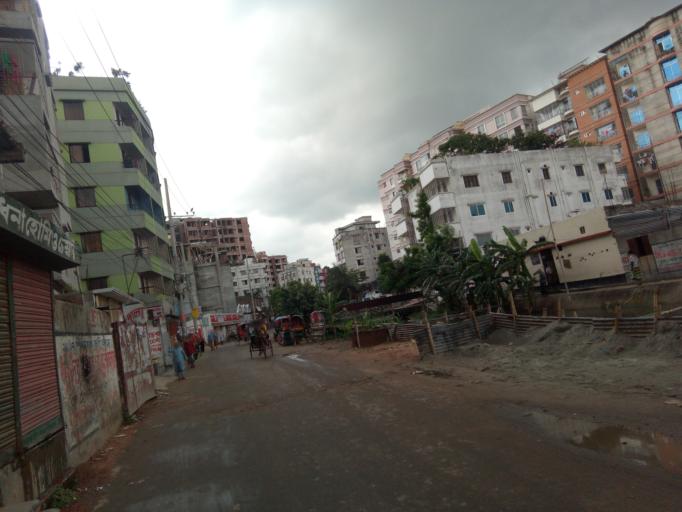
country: BD
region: Dhaka
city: Azimpur
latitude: 23.7623
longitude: 90.3537
